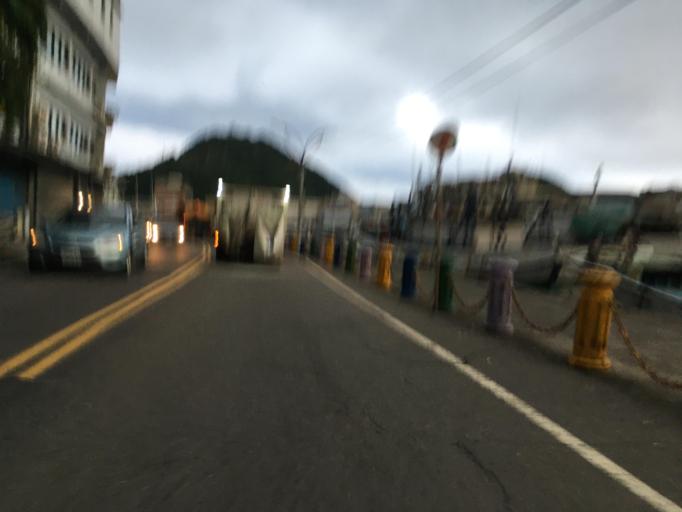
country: TW
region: Taiwan
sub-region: Yilan
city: Yilan
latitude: 24.5790
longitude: 121.8698
